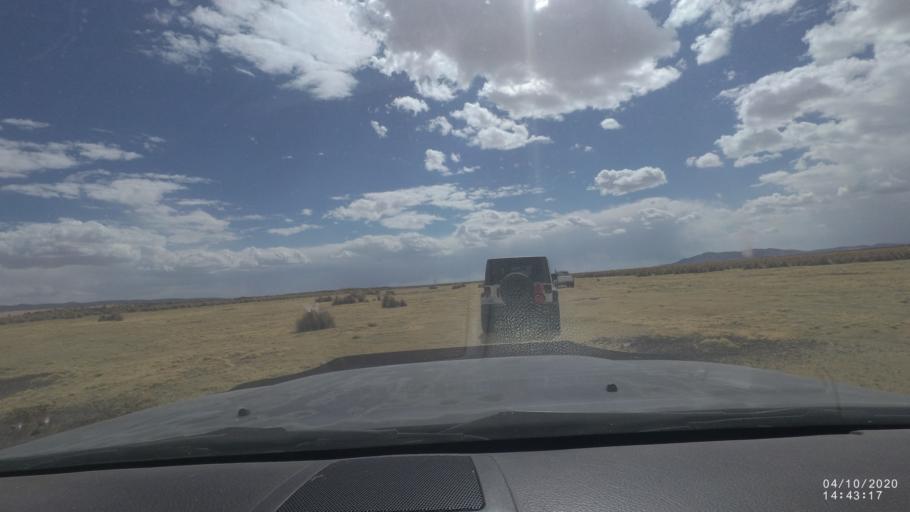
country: BO
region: Oruro
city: Poopo
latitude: -18.6867
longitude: -67.4929
